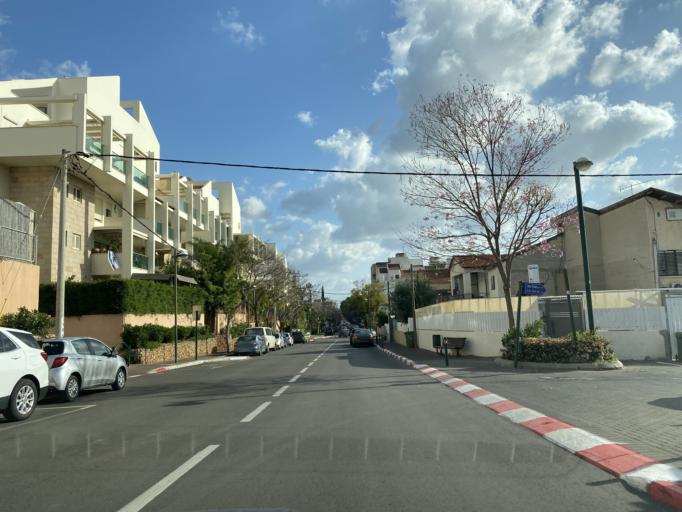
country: IL
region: Central District
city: Kfar Saba
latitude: 32.1814
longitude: 34.9194
